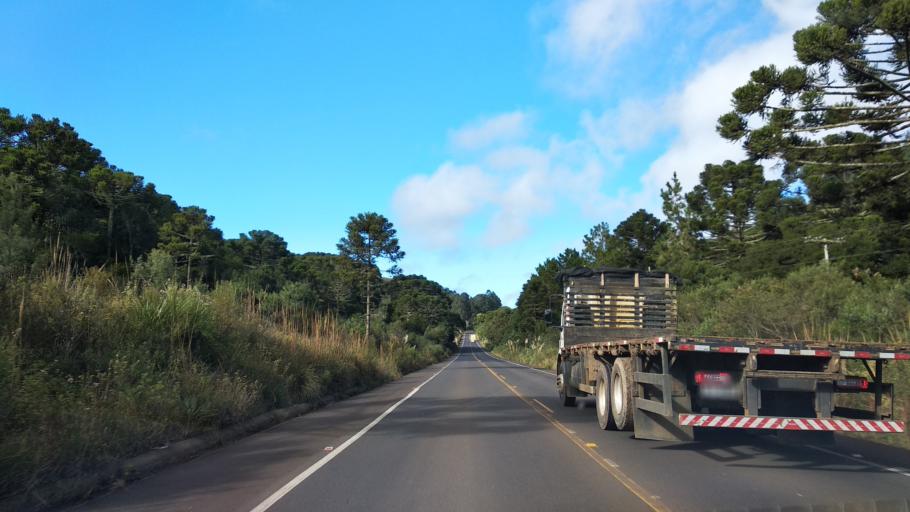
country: BR
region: Santa Catarina
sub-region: Lages
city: Lages
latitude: -27.9518
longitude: -50.0956
